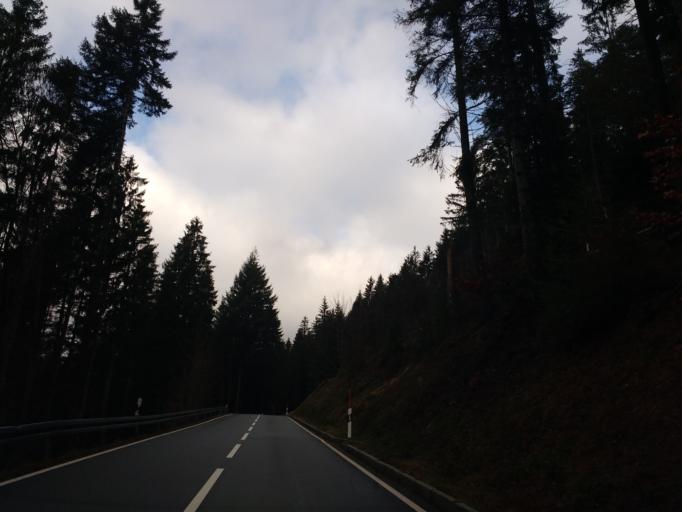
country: DE
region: Baden-Wuerttemberg
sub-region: Karlsruhe Region
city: Bad Rippoldsau-Schapbach
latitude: 48.4523
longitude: 8.2901
